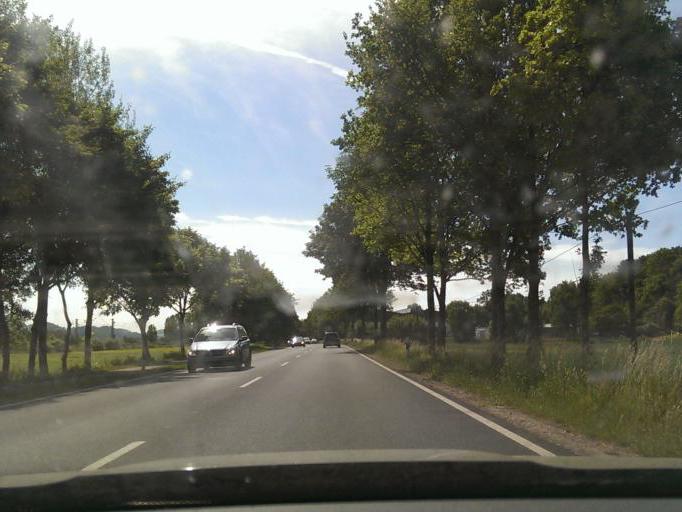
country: DE
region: Lower Saxony
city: Bruggen
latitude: 52.0295
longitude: 9.7690
